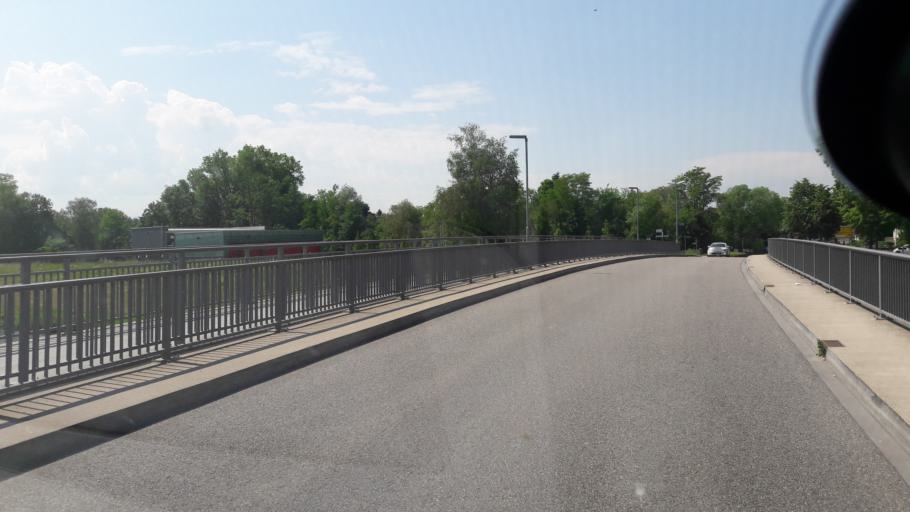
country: DE
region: Baden-Wuerttemberg
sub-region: Karlsruhe Region
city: Rastatt
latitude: 48.8452
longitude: 8.2214
